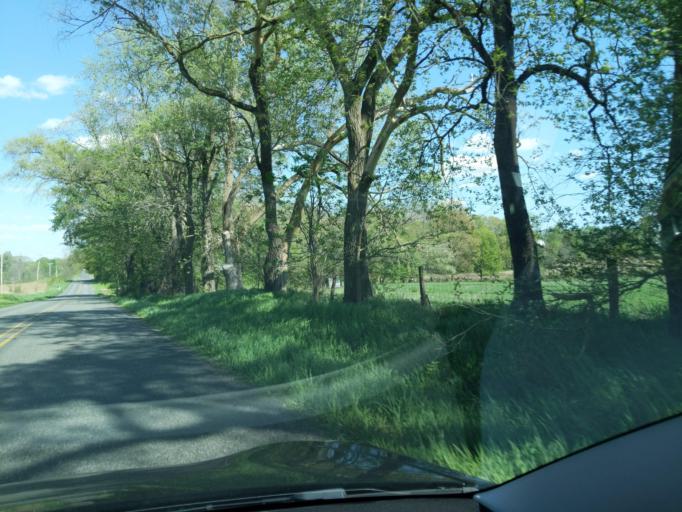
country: US
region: Michigan
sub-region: Barry County
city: Middleville
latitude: 42.7981
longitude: -85.3950
